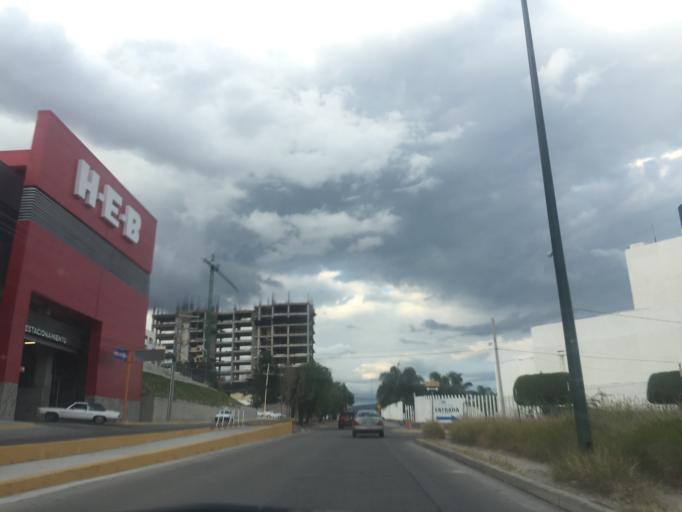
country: MX
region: Guanajuato
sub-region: Leon
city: La Ermita
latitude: 21.1566
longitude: -101.7019
